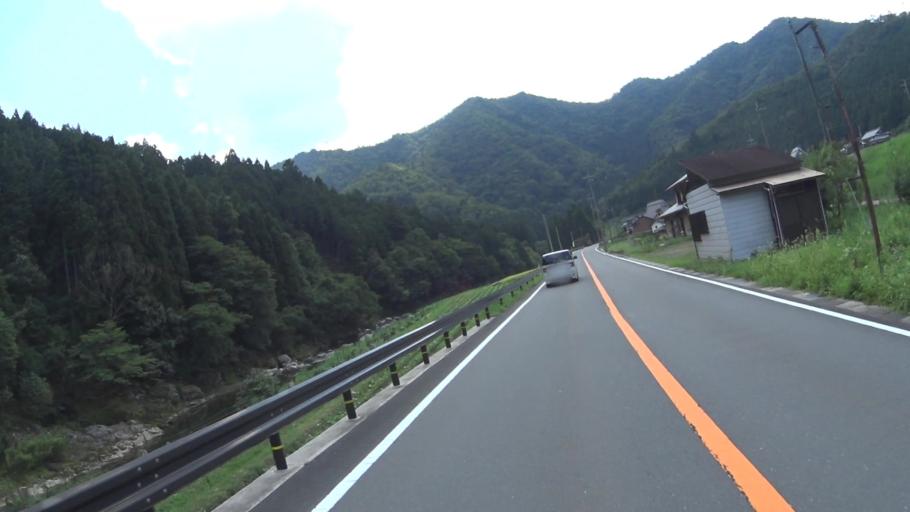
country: JP
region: Kyoto
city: Maizuru
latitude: 35.2896
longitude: 135.5561
